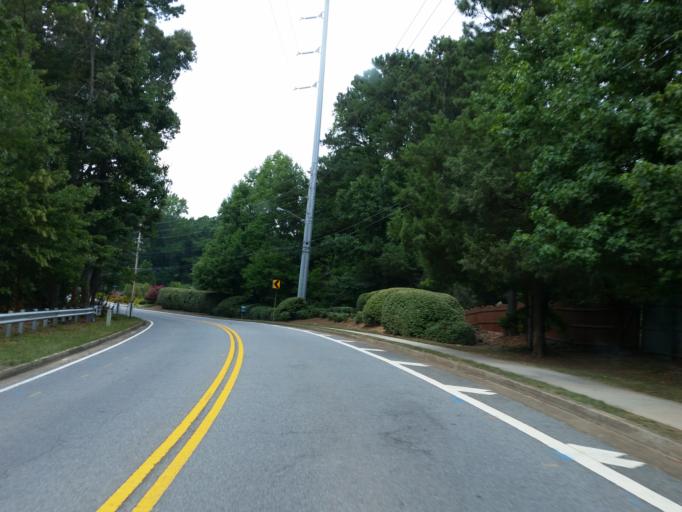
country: US
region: Georgia
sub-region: Fulton County
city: Roswell
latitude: 34.0453
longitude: -84.4182
